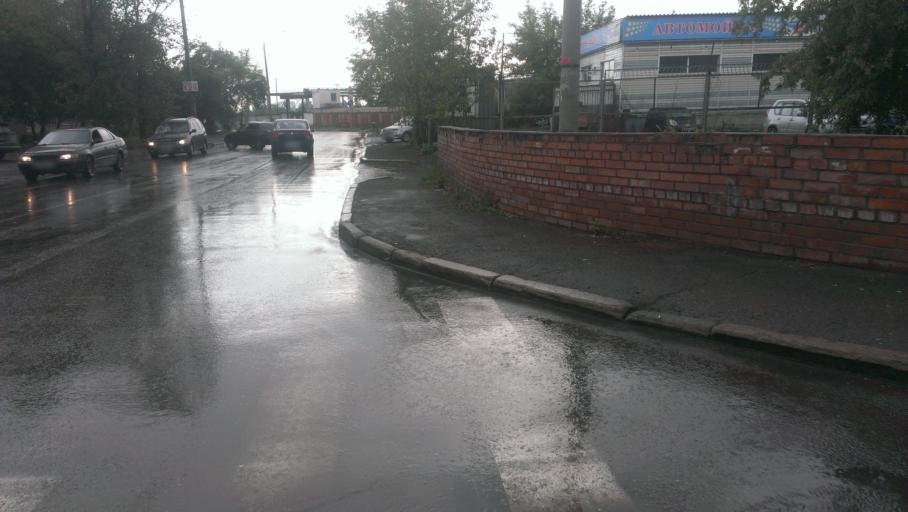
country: RU
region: Altai Krai
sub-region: Gorod Barnaulskiy
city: Barnaul
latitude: 53.3609
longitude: 83.7628
